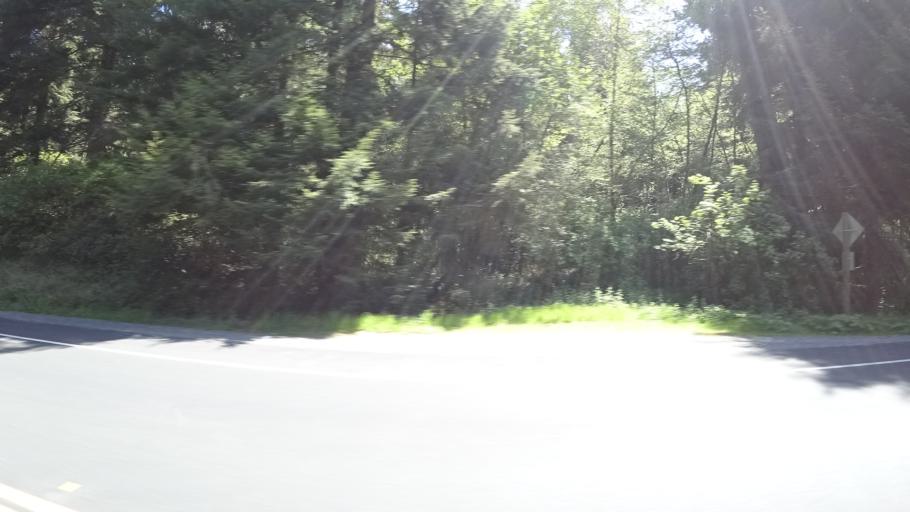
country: US
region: California
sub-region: Humboldt County
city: Westhaven-Moonstone
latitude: 41.1710
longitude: -124.1019
